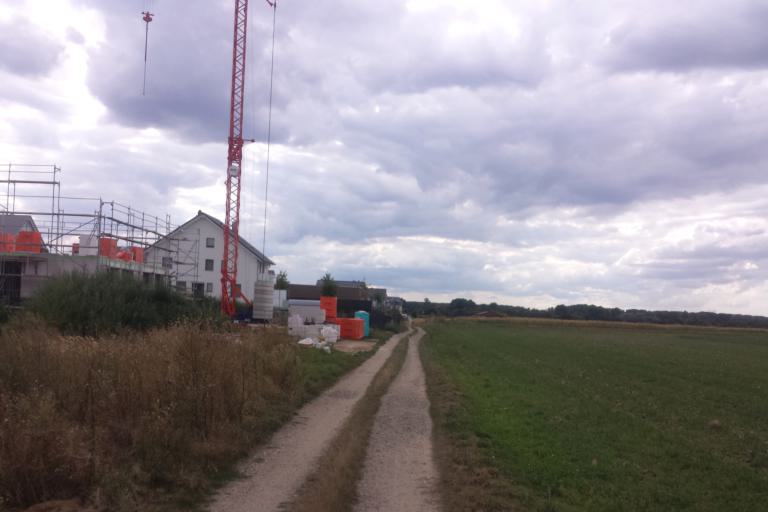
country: DE
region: Hesse
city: Lampertheim
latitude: 49.5503
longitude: 8.4445
